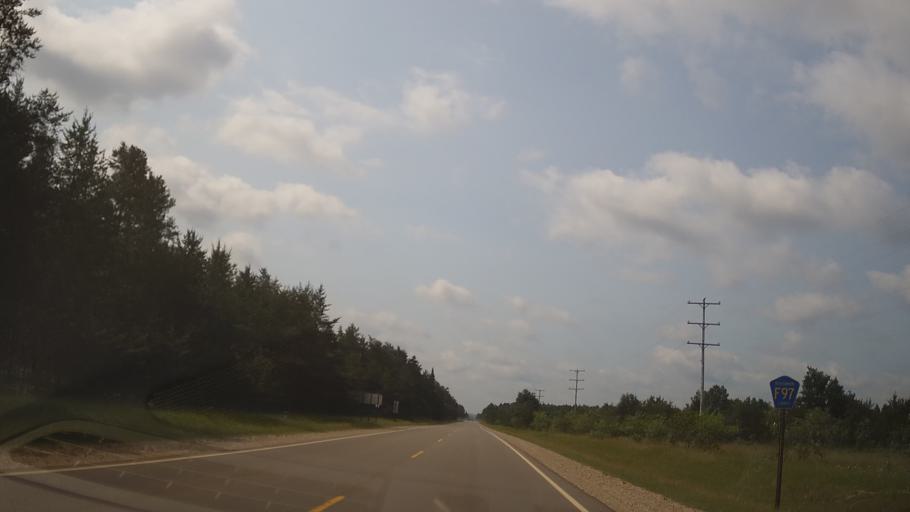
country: US
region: Michigan
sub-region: Roscommon County
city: Saint Helen
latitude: 44.4064
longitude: -84.4104
